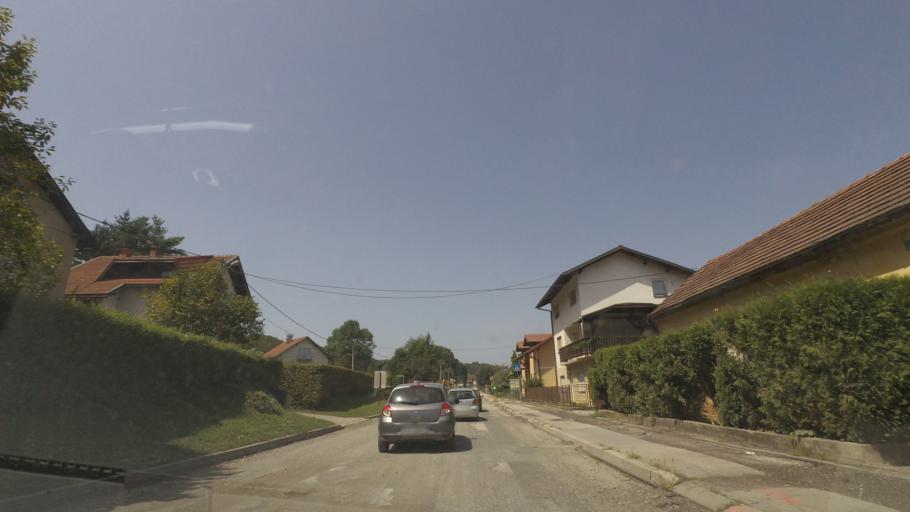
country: HR
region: Karlovacka
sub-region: Grad Karlovac
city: Karlovac
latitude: 45.4990
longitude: 15.5270
